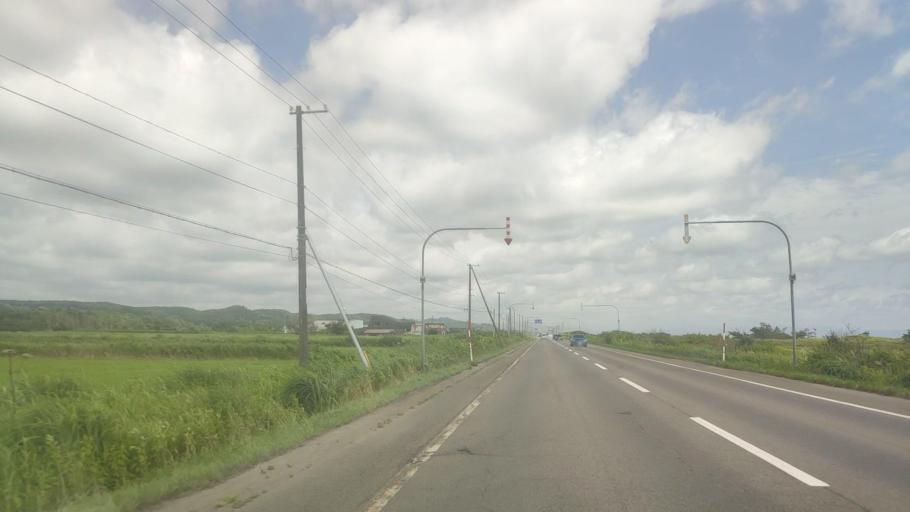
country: JP
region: Hokkaido
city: Niseko Town
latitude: 42.3927
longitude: 140.2992
